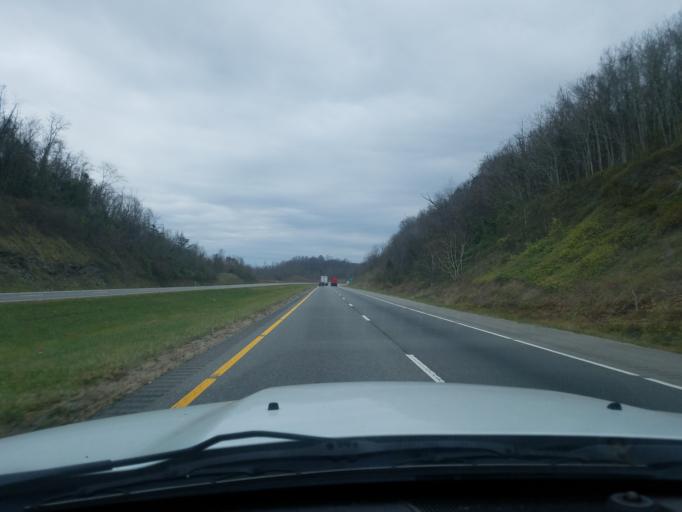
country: US
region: Kentucky
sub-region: Boyd County
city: Catlettsburg
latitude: 38.3809
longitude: -82.6562
